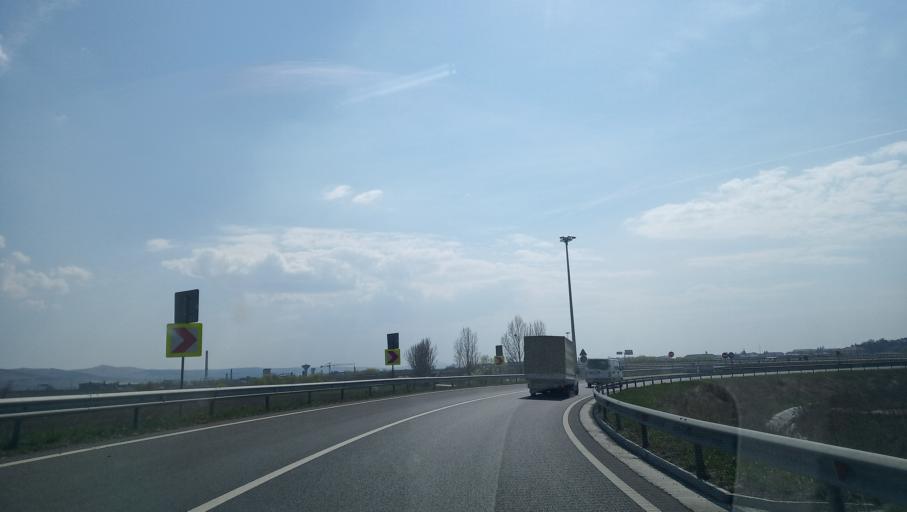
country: RO
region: Alba
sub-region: Municipiul Aiud
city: Aiud
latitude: 46.3287
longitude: 23.7327
